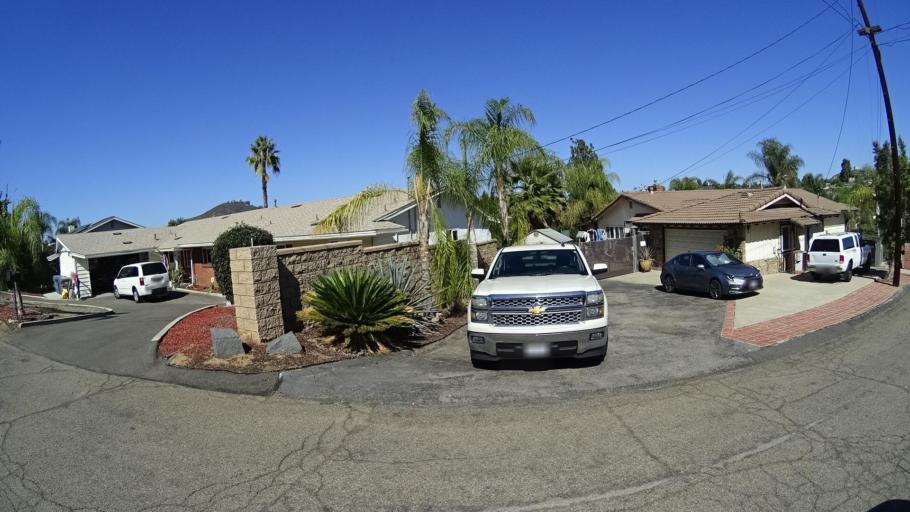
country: US
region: California
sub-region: San Diego County
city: Winter Gardens
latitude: 32.8187
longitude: -116.9242
